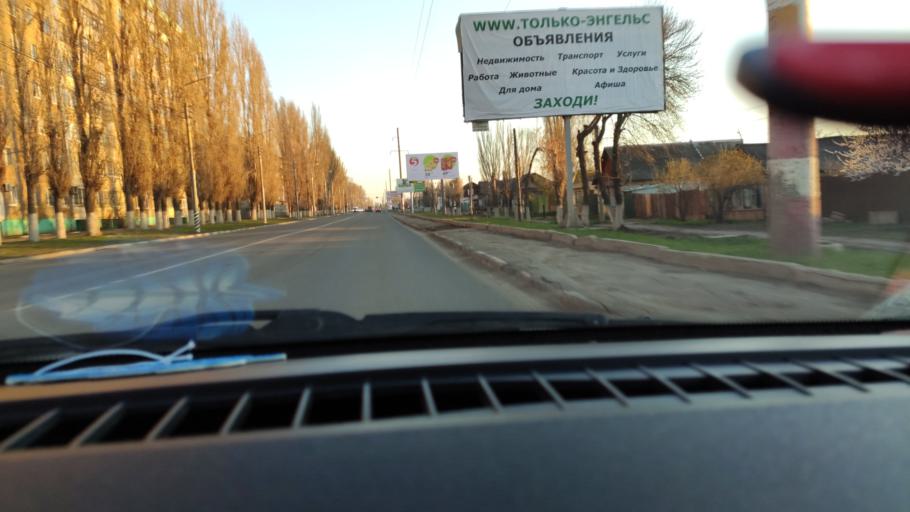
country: RU
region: Saratov
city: Privolzhskiy
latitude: 51.4080
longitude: 46.0402
